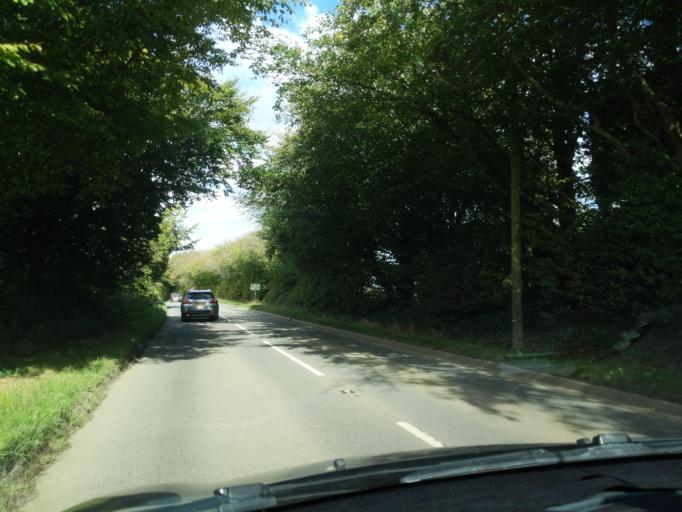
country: GB
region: England
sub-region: Devon
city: Holsworthy
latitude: 50.8523
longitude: -4.3321
